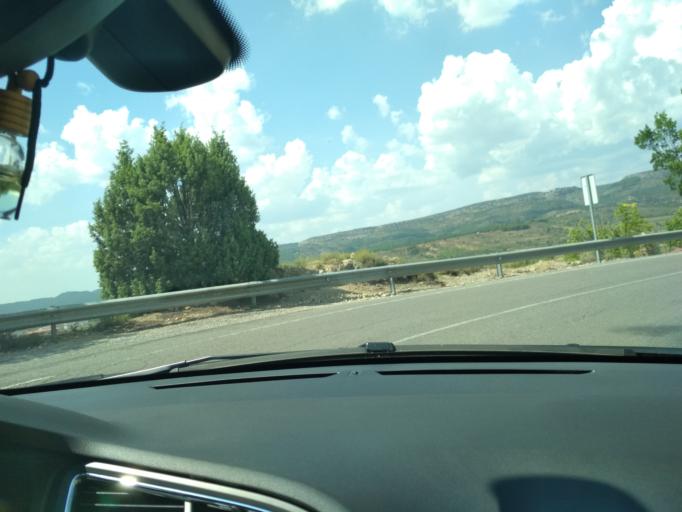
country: ES
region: Aragon
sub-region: Provincia de Teruel
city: Rubielos de Mora
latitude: 40.1870
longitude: -0.6511
